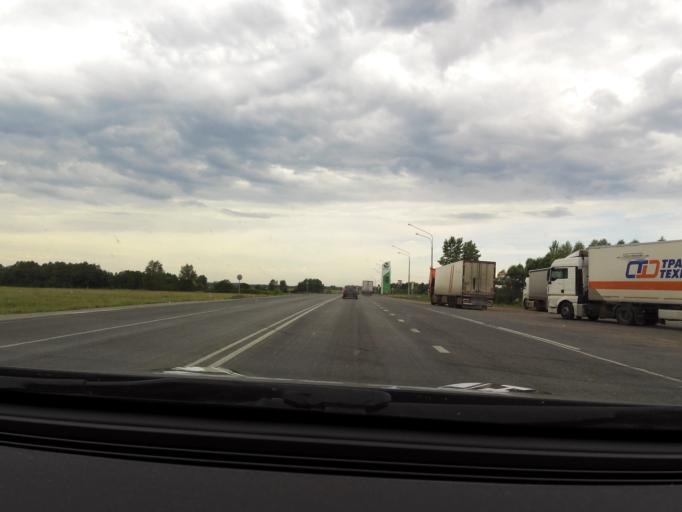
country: RU
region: Bashkortostan
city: Kudeyevskiy
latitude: 54.8168
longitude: 56.7362
